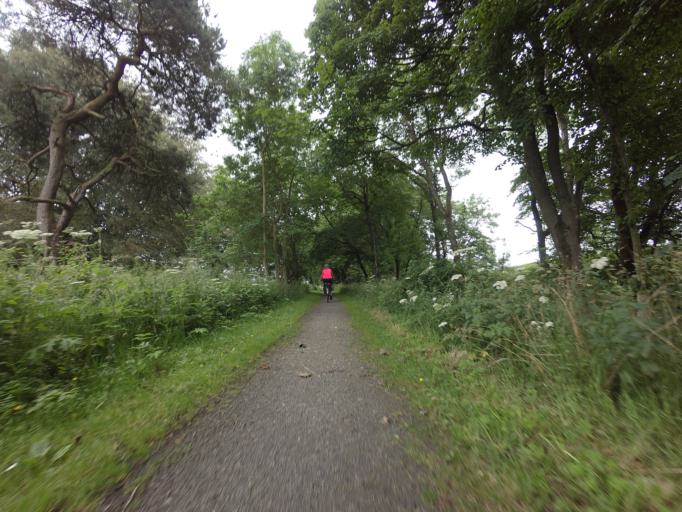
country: GB
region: Scotland
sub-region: Aberdeenshire
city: Ellon
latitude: 57.4760
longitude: -2.1281
